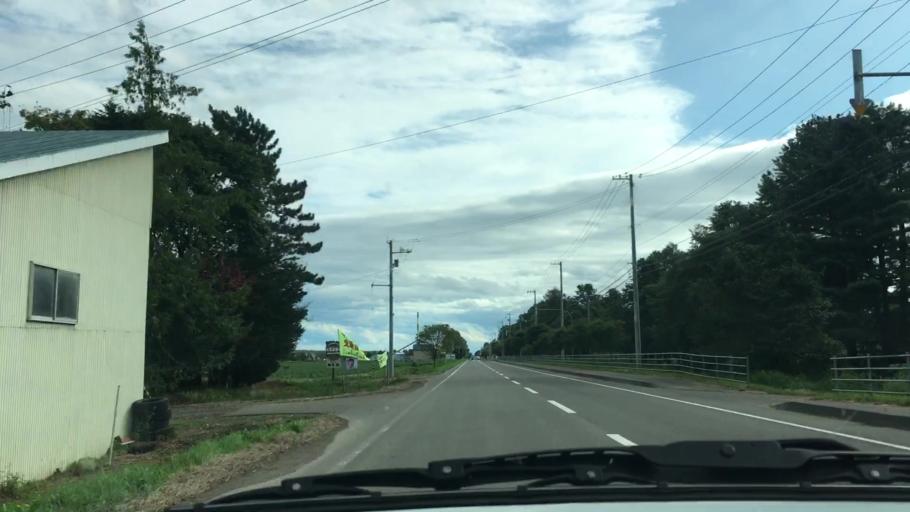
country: JP
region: Hokkaido
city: Otofuke
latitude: 43.2477
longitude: 143.2985
